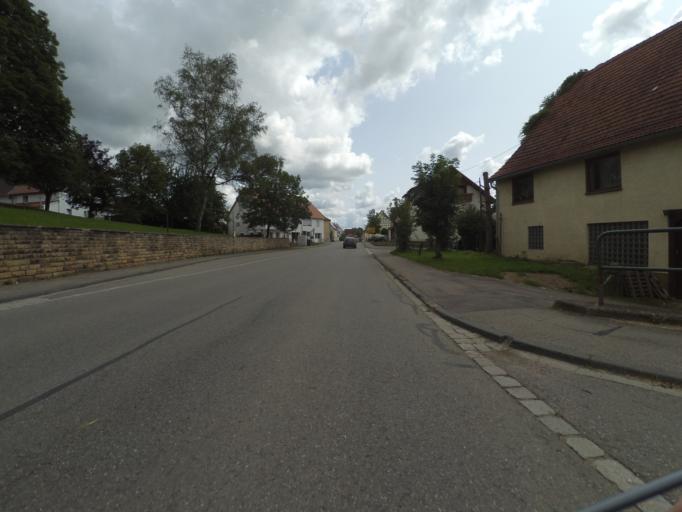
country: DE
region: Baden-Wuerttemberg
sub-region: Freiburg Region
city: Donaueschingen
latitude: 47.9391
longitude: 8.5511
